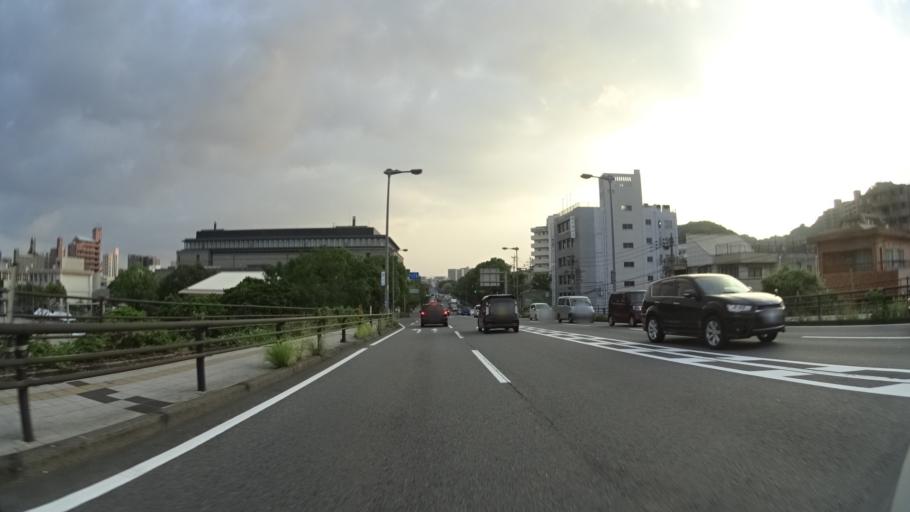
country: JP
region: Kagoshima
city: Kagoshima-shi
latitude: 31.6014
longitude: 130.5583
